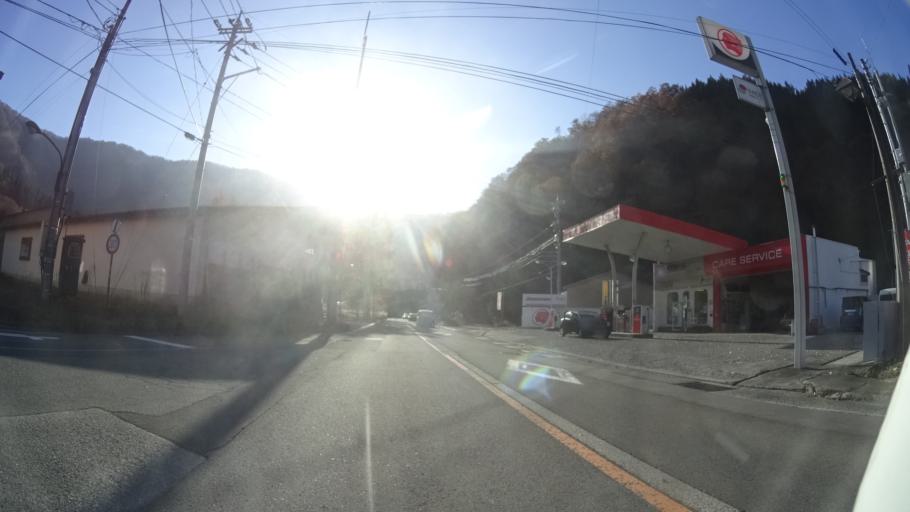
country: JP
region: Fukui
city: Ono
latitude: 35.9021
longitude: 136.6577
